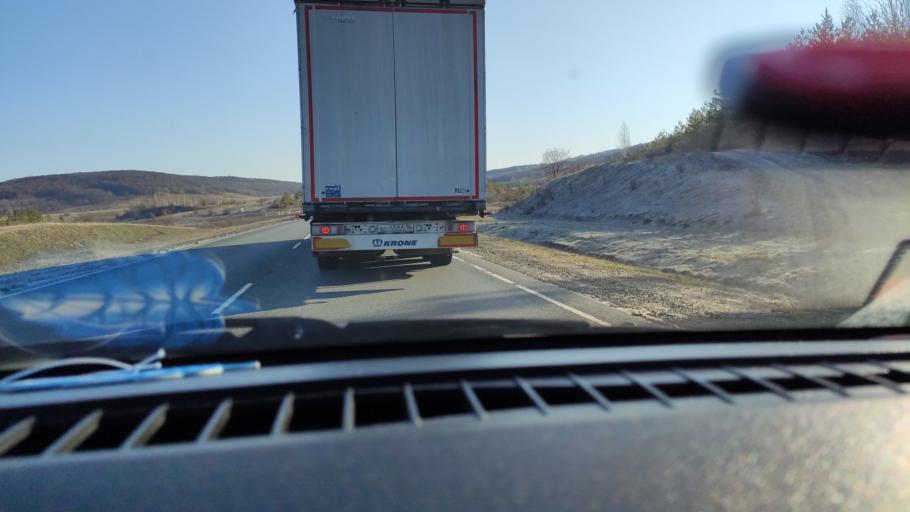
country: RU
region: Saratov
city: Alekseyevka
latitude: 52.3951
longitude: 47.9810
